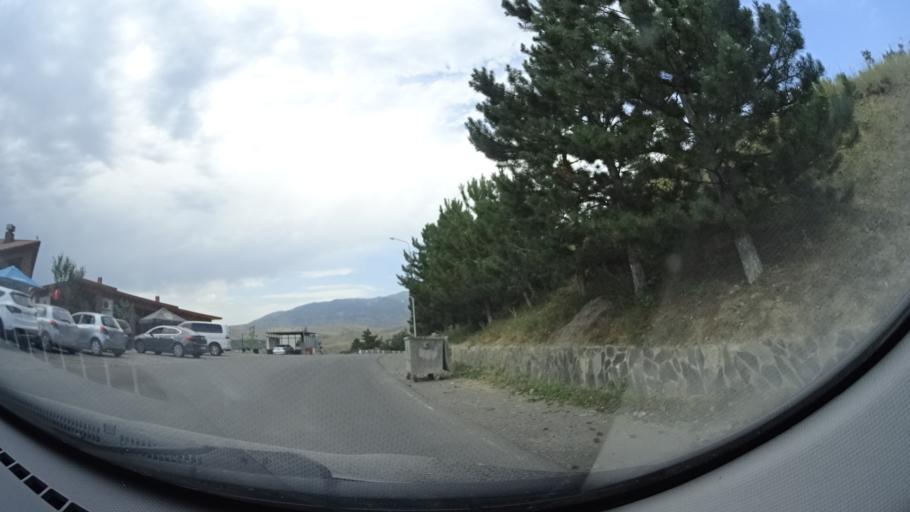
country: GE
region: Samtskhe-Javakheti
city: Aspindza
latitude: 41.5781
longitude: 43.2435
